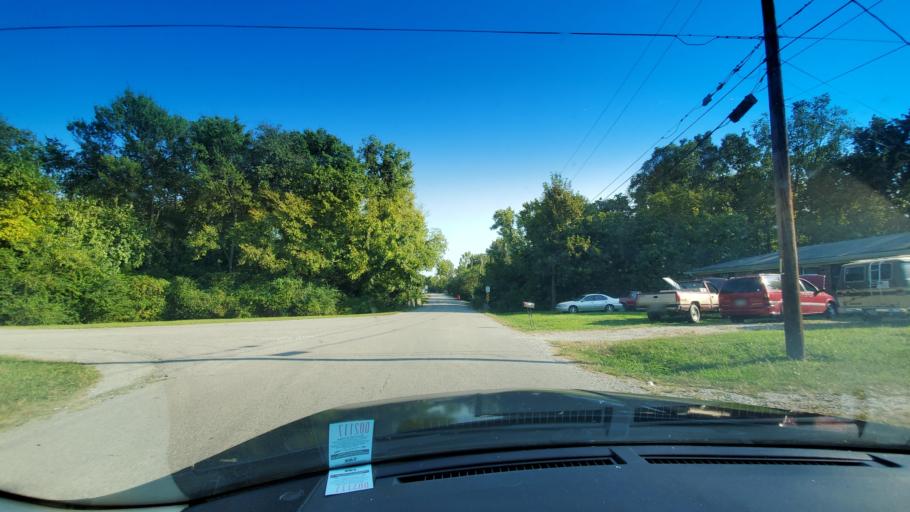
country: US
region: Tennessee
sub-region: Smith County
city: Carthage
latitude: 36.2544
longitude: -85.9568
